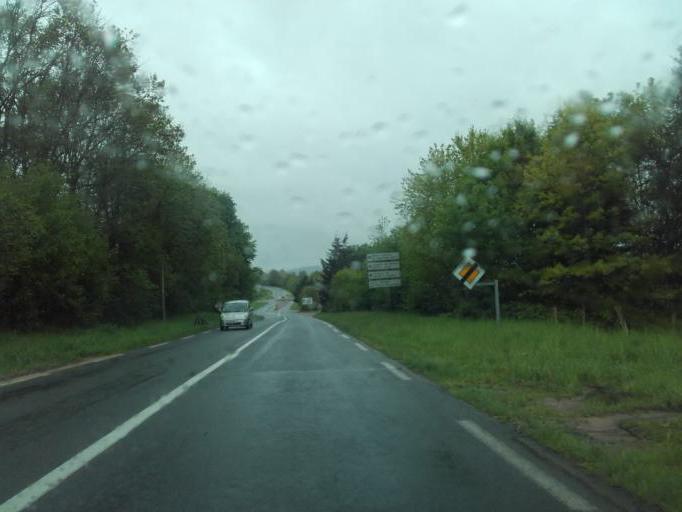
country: FR
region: Bourgogne
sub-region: Departement de Saone-et-Loire
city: Cluny
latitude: 46.4045
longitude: 4.6550
